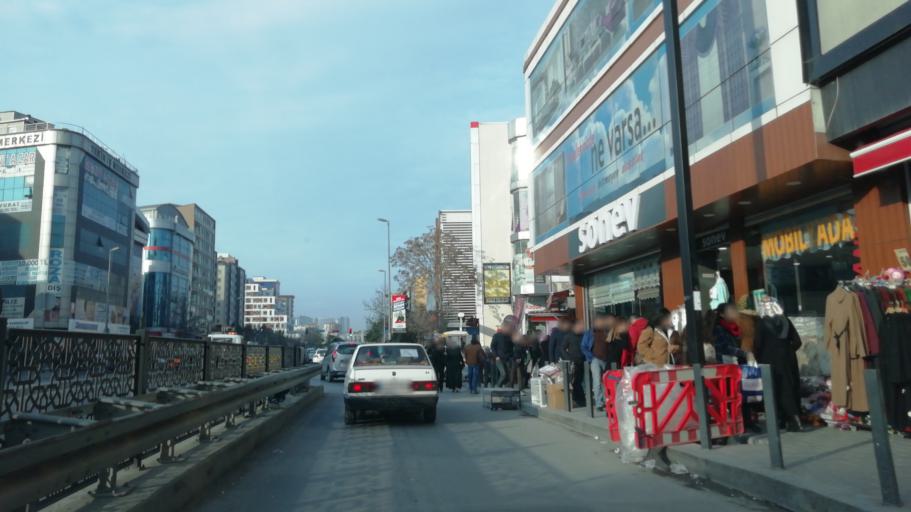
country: TR
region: Istanbul
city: Esenyurt
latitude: 41.0363
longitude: 28.6791
